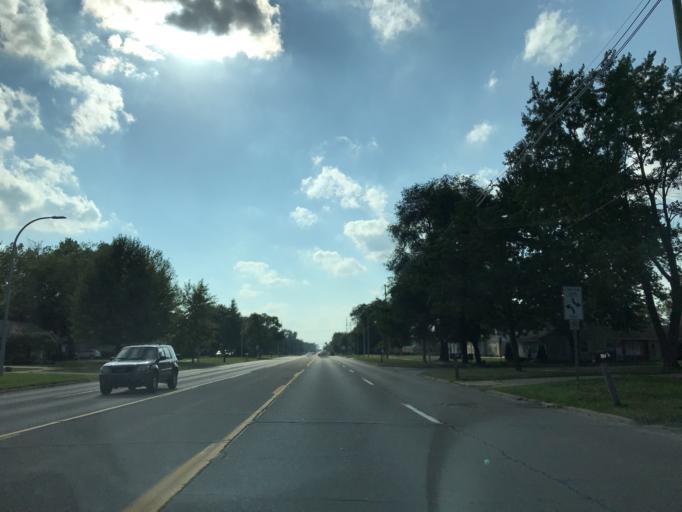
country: US
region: Michigan
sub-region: Wayne County
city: Livonia
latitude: 42.3980
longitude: -83.3406
